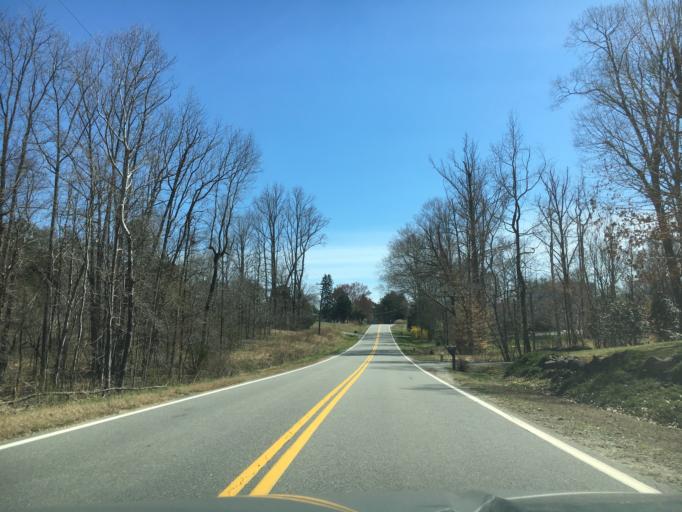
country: US
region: Virginia
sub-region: Halifax County
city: Halifax
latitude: 36.7621
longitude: -78.9125
